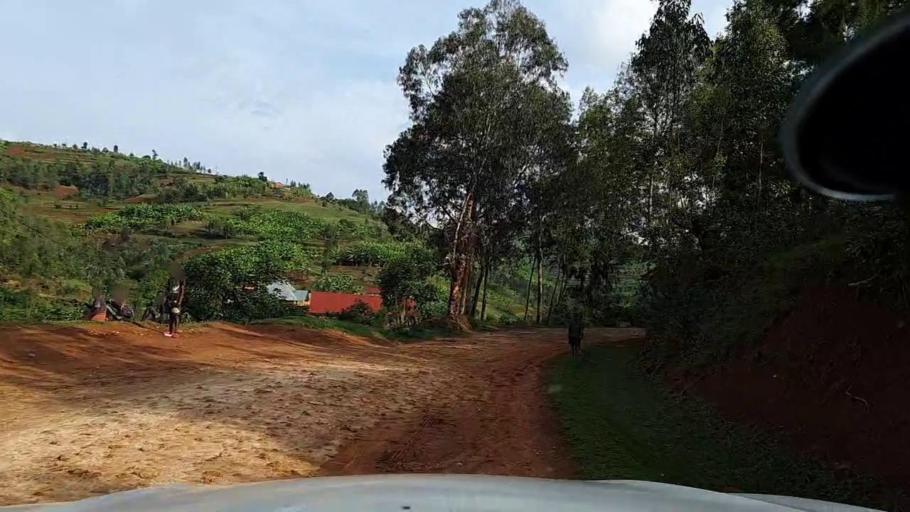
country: RW
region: Southern Province
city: Gitarama
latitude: -2.1640
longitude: 29.5579
